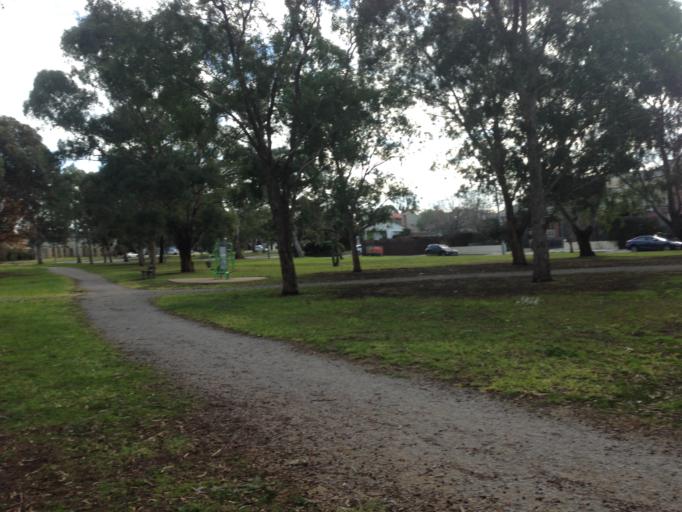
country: AU
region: Victoria
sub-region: Banyule
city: Bellfield
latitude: -37.7579
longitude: 145.0427
